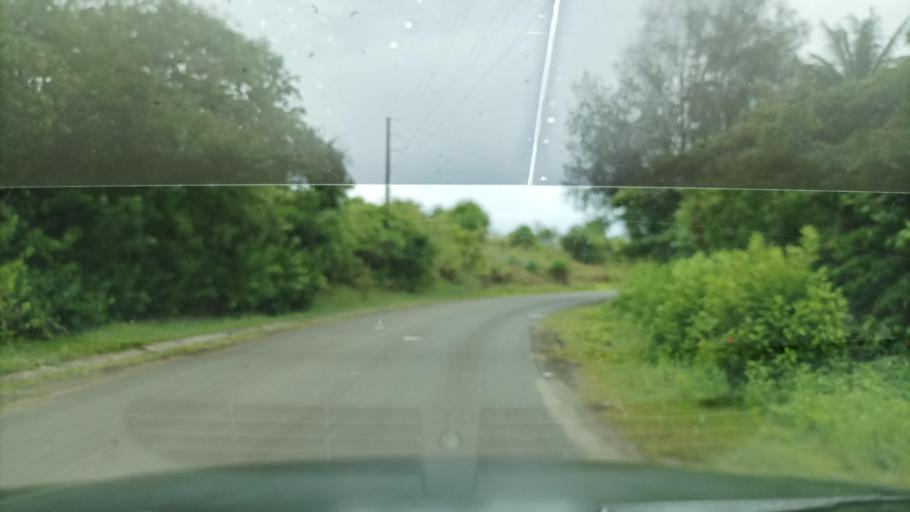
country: FM
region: Yap
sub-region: Weloy Municipality
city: Colonia
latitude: 9.5481
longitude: 138.1573
